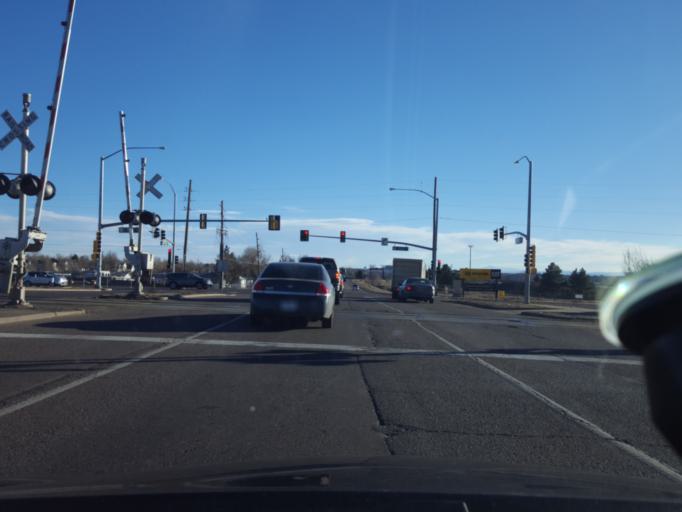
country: US
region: Colorado
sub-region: Adams County
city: Aurora
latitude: 39.7545
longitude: -104.7723
